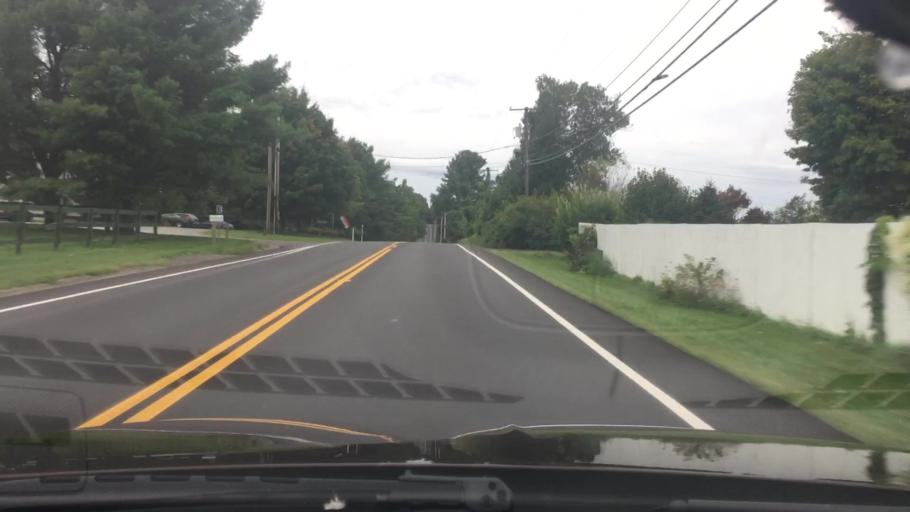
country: US
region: New York
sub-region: Dutchess County
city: Millbrook
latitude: 41.8220
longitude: -73.6236
